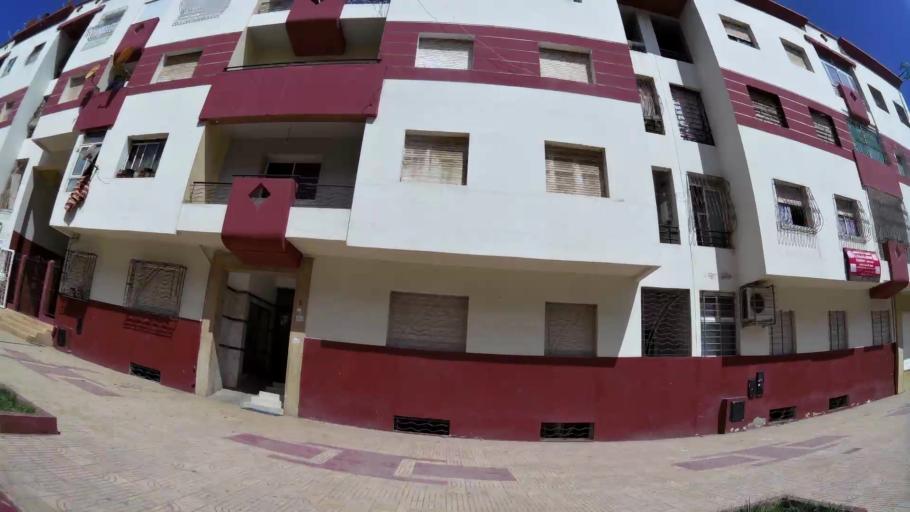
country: MA
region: Rabat-Sale-Zemmour-Zaer
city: Sale
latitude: 34.0772
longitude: -6.7909
